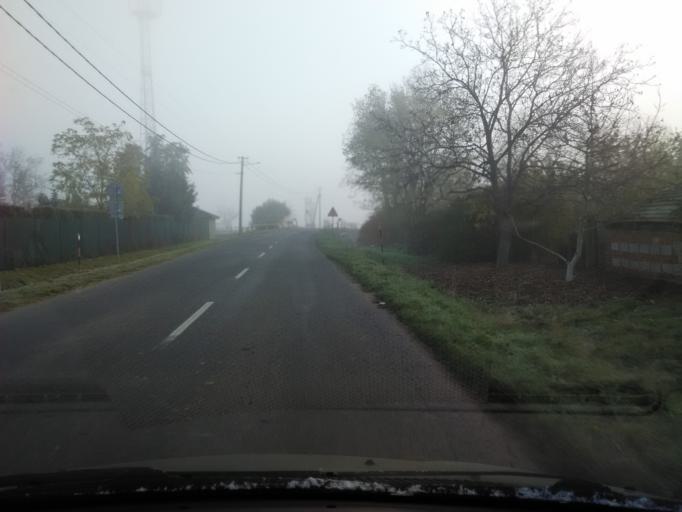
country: SK
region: Nitriansky
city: Tlmace
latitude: 48.2446
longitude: 18.5419
